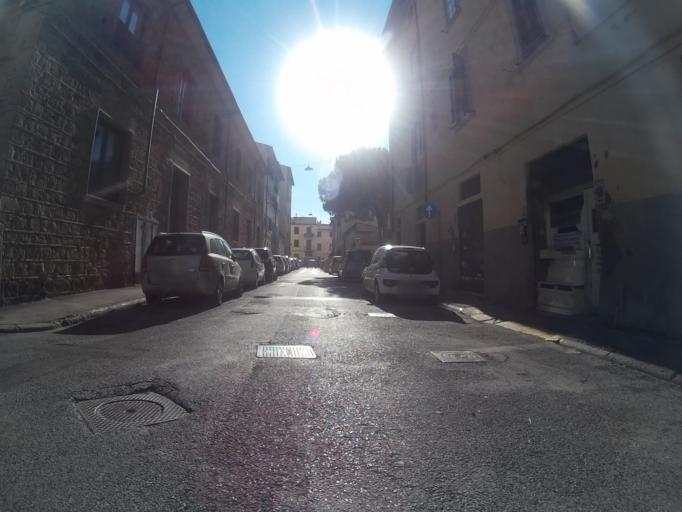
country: IT
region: Tuscany
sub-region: Provincia di Livorno
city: Livorno
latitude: 43.5575
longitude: 10.3125
